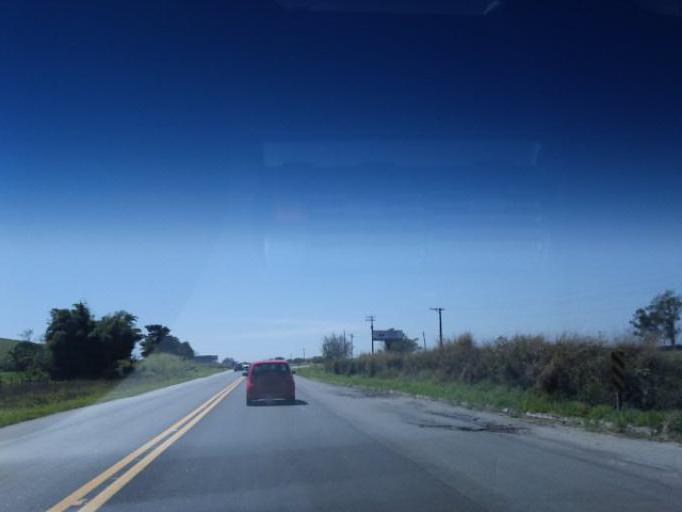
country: BR
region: Sao Paulo
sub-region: Tremembe
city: Tremembe
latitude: -22.9520
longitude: -45.6182
